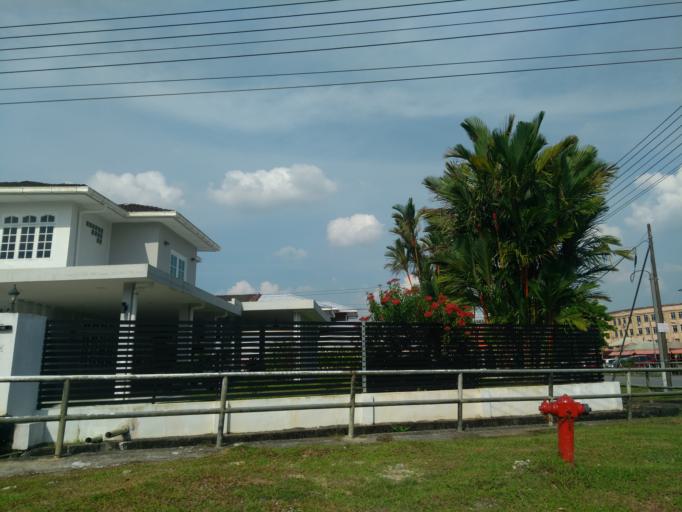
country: MY
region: Sarawak
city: Kuching
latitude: 1.5756
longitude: 110.2937
